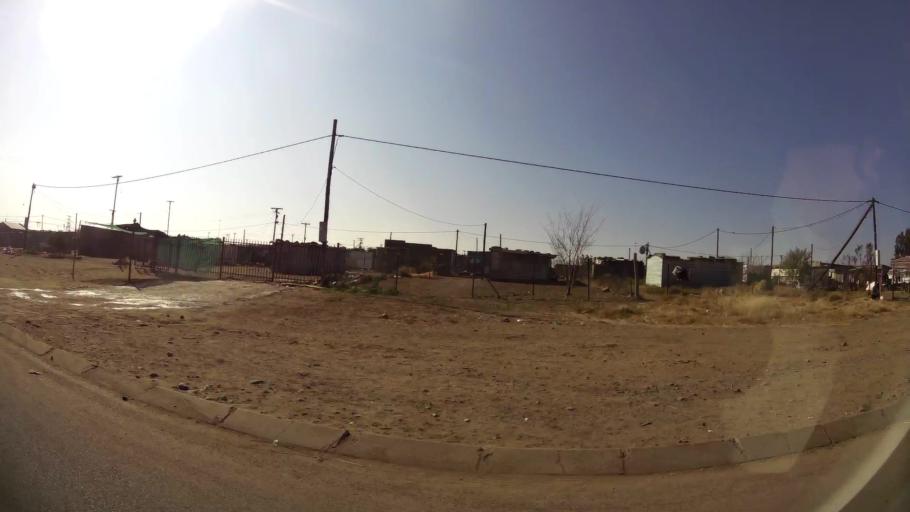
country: ZA
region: Orange Free State
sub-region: Mangaung Metropolitan Municipality
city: Bloemfontein
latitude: -29.1750
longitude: 26.2409
